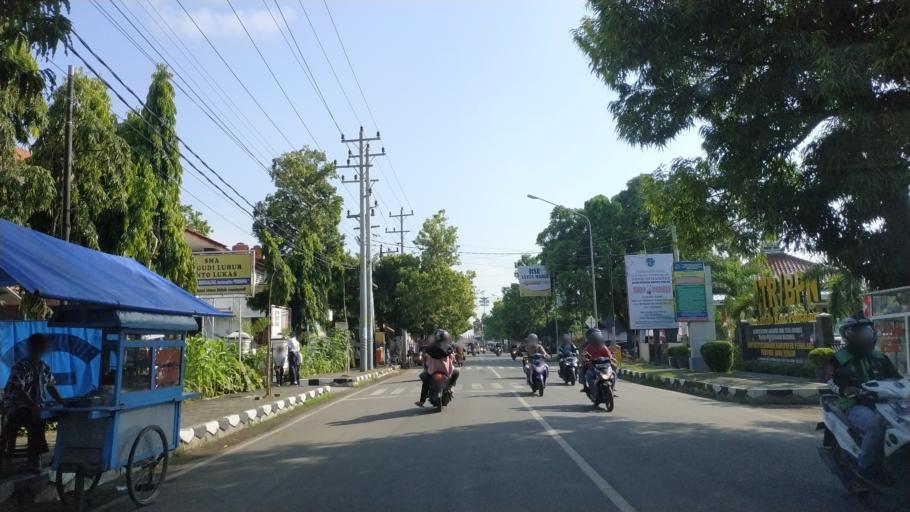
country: ID
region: Central Java
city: Pemalang
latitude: -6.8954
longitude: 109.3881
